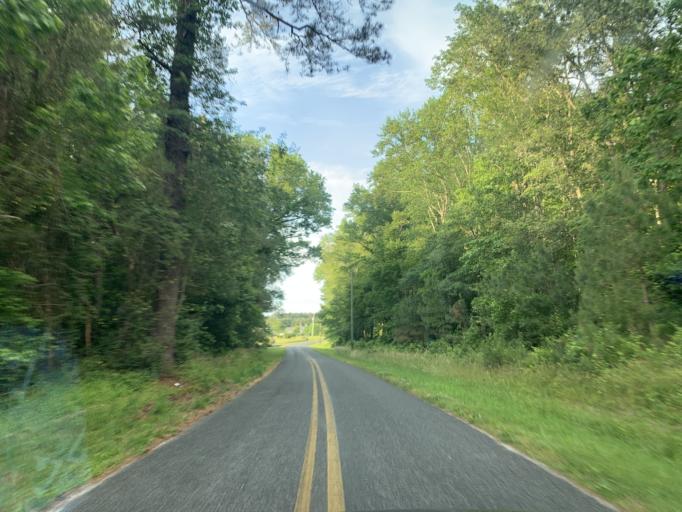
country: US
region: Maryland
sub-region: Worcester County
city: Pocomoke City
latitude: 38.0858
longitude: -75.4669
